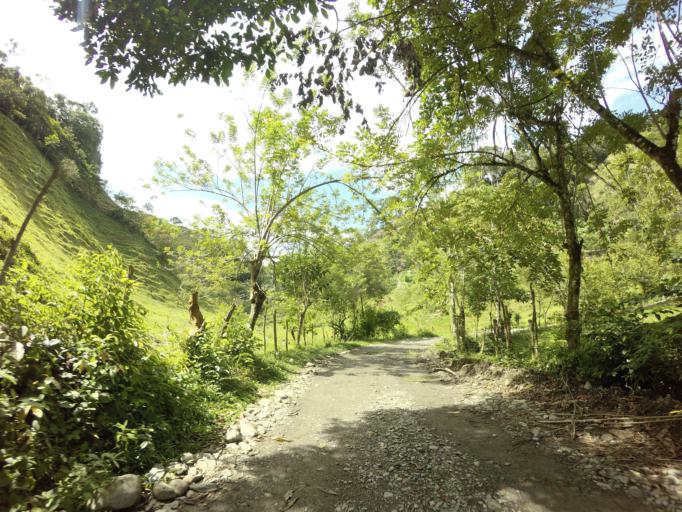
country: CO
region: Antioquia
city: Narino
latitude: 5.5402
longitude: -75.1328
